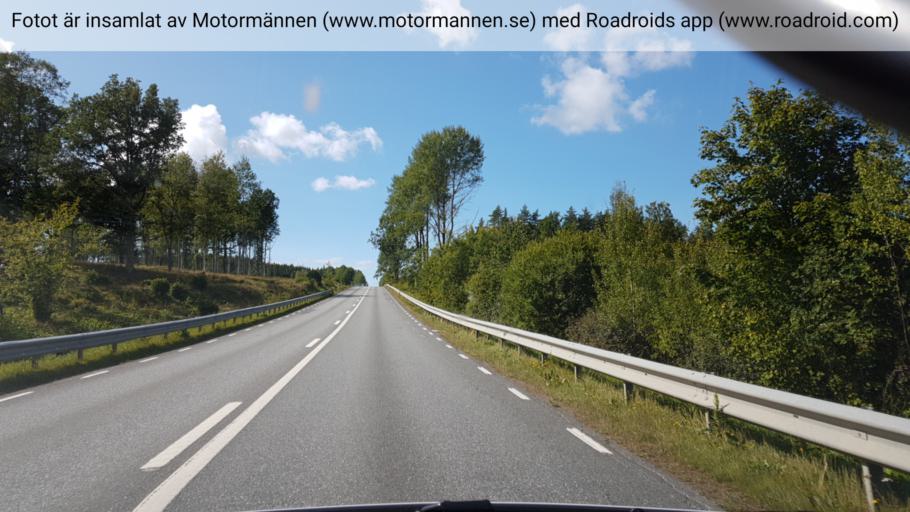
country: SE
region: Joenkoeping
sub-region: Jonkopings Kommun
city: Asa
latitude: 58.0126
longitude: 14.6653
